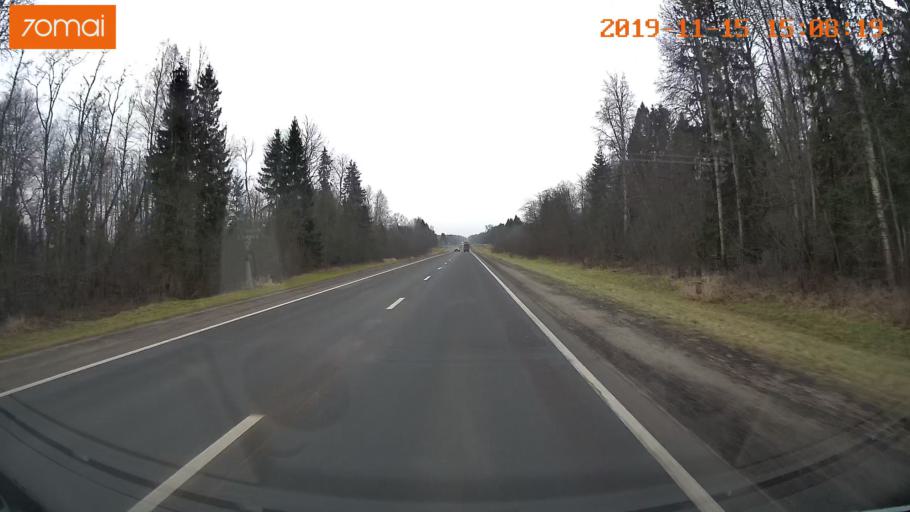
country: RU
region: Jaroslavl
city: Prechistoye
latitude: 58.3726
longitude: 40.2784
